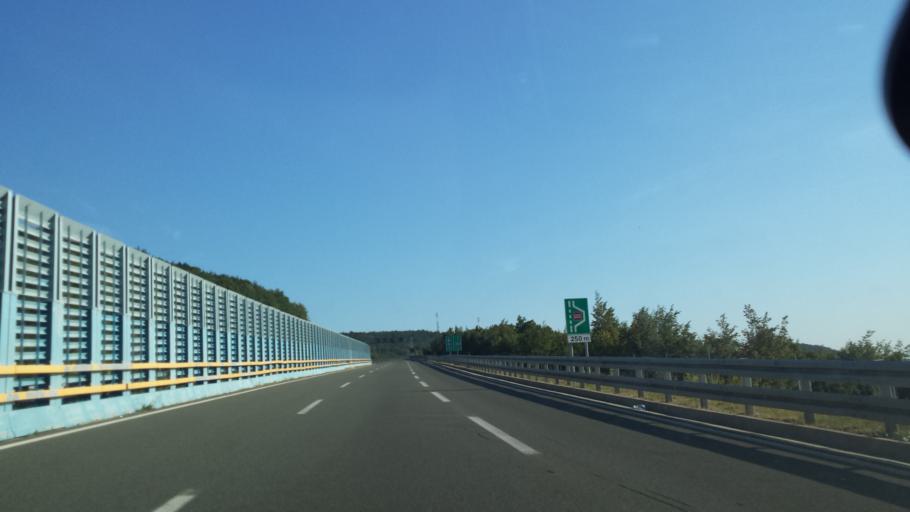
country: HR
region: Primorsko-Goranska
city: Krasica
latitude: 45.3438
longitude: 14.5936
